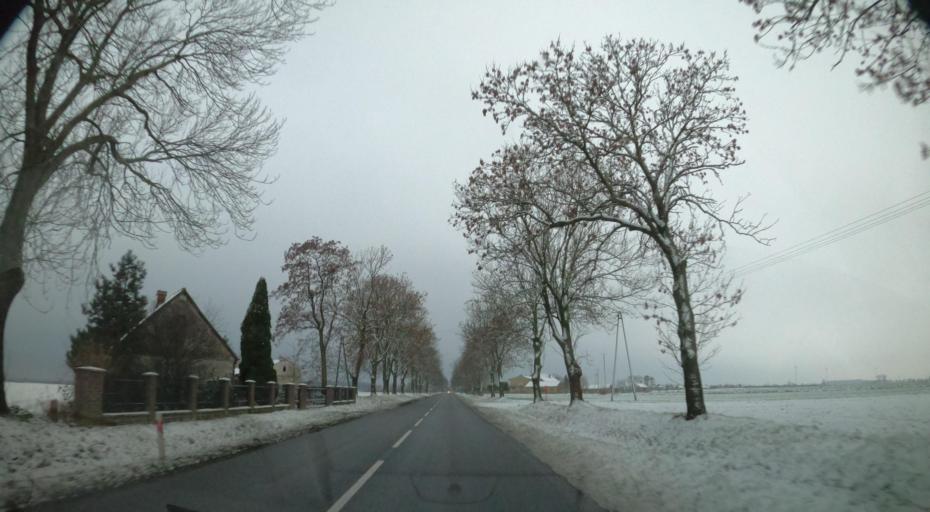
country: PL
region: Kujawsko-Pomorskie
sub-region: Powiat lipnowski
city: Dobrzyn nad Wisla
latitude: 52.6433
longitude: 19.3385
